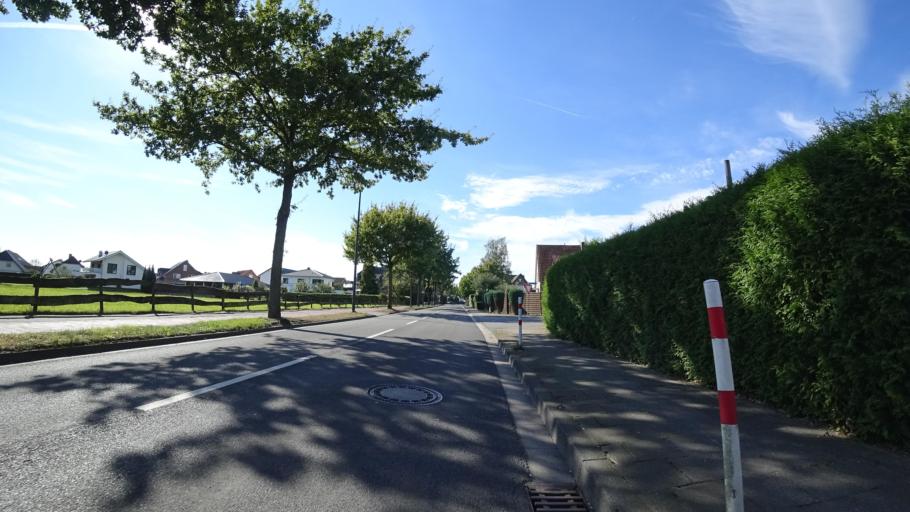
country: DE
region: North Rhine-Westphalia
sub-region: Regierungsbezirk Detmold
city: Guetersloh
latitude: 51.9246
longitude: 8.4319
